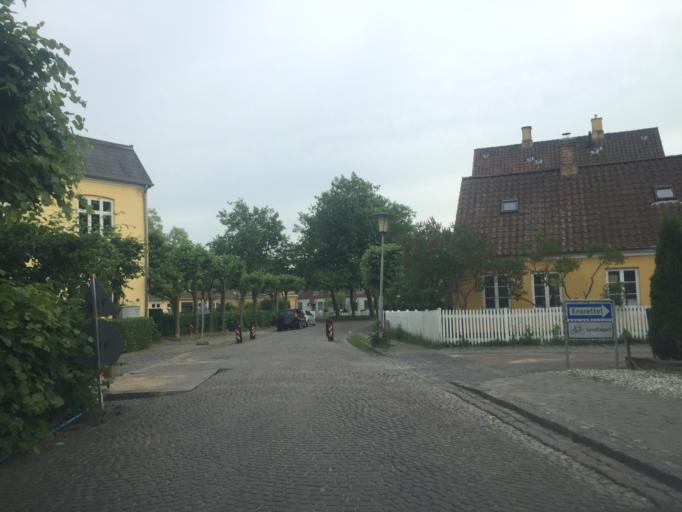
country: DK
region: Capital Region
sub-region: Lyngby-Tarbaek Kommune
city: Kongens Lyngby
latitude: 55.7773
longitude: 12.5045
